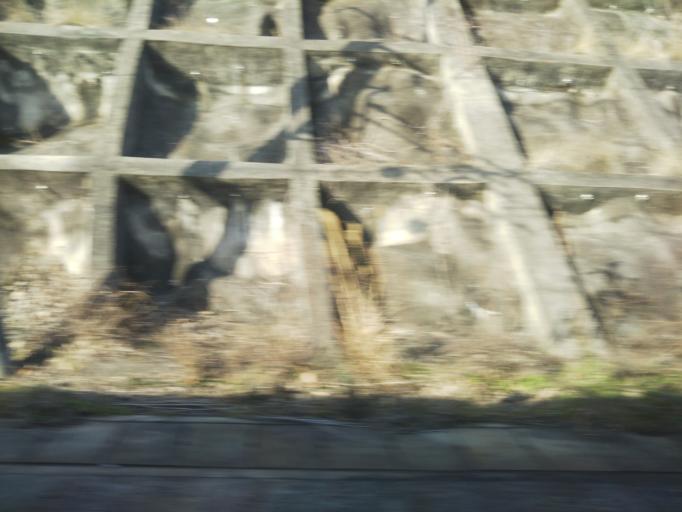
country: JP
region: Kagawa
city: Sakaidecho
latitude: 34.4460
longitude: 133.8083
